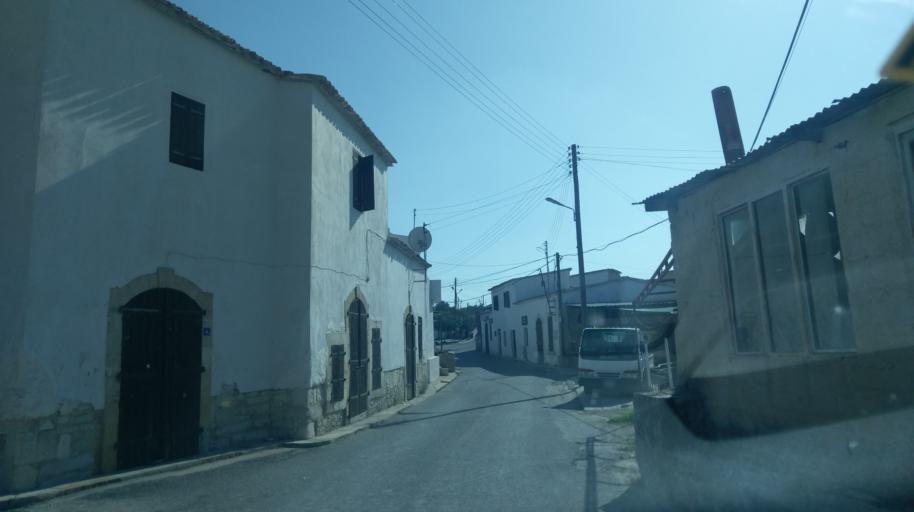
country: CY
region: Lefkosia
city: Lympia
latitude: 35.0119
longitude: 33.4649
